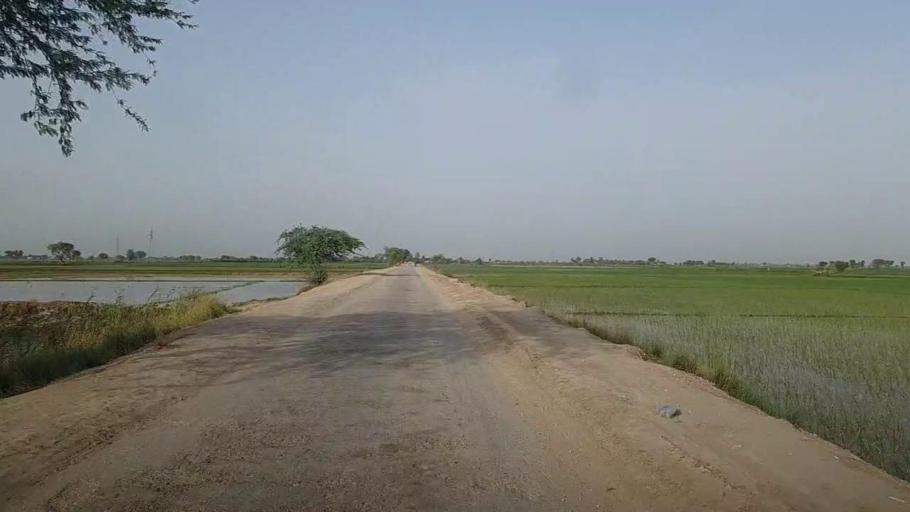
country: PK
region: Sindh
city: Mehar
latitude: 27.1548
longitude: 67.8047
